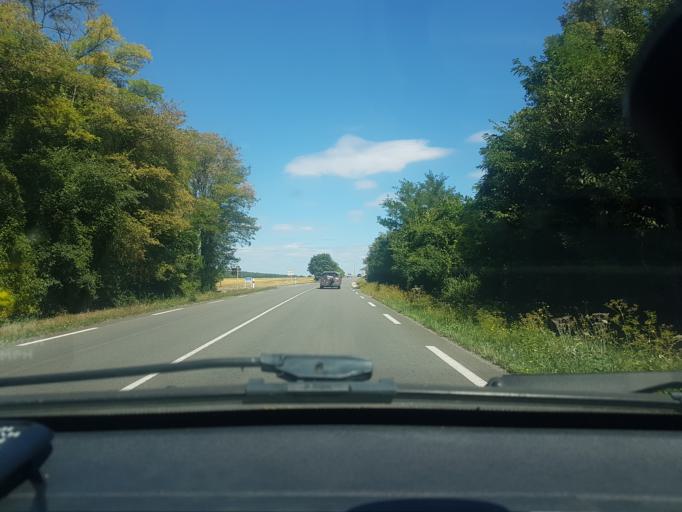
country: FR
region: Bourgogne
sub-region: Departement de la Cote-d'Or
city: Belleneuve
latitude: 47.3633
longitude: 5.2231
